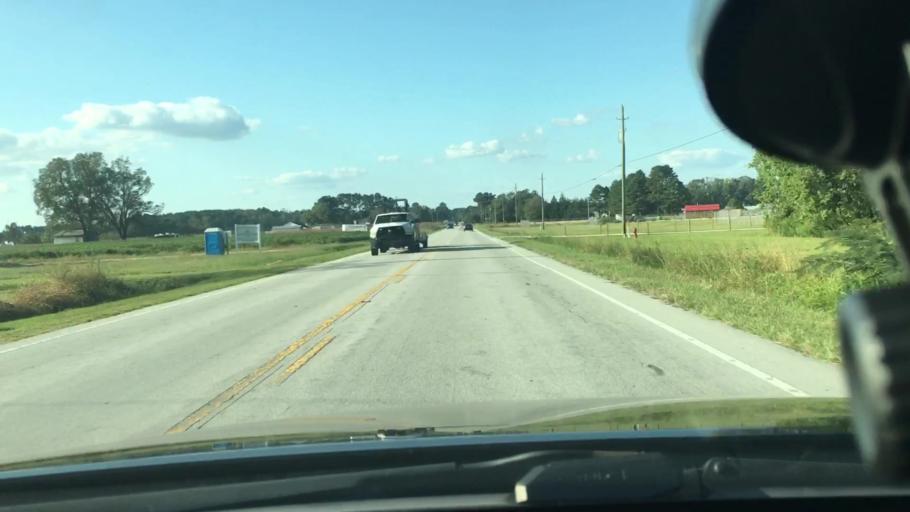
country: US
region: North Carolina
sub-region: Pitt County
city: Windsor
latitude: 35.5005
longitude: -77.3125
